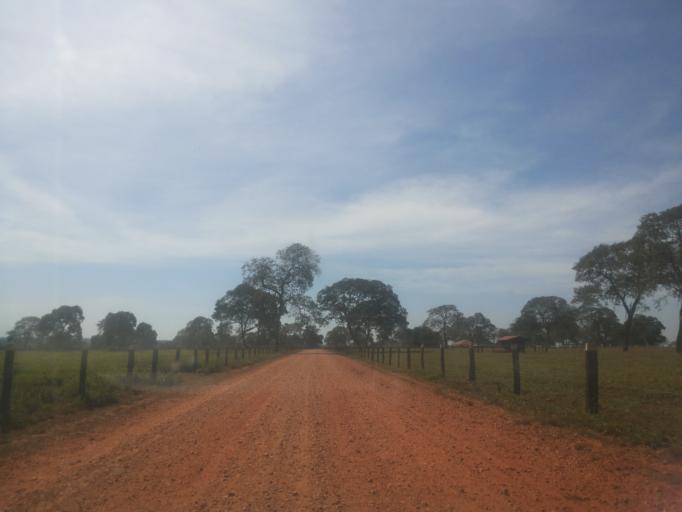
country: BR
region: Minas Gerais
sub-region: Santa Vitoria
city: Santa Vitoria
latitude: -19.0092
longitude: -50.4292
